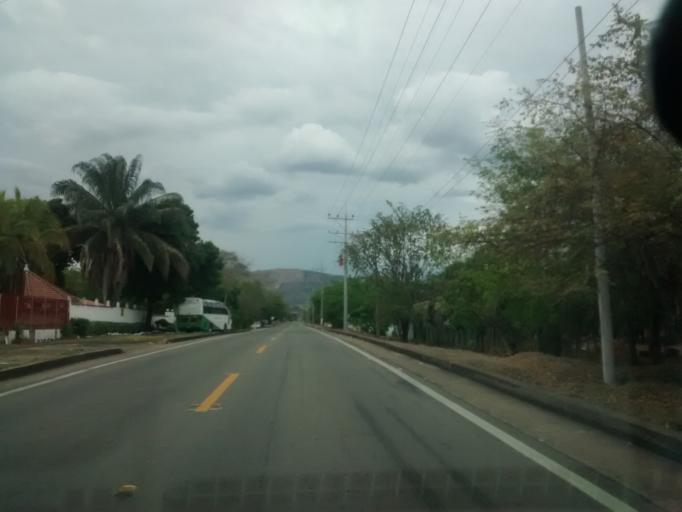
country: CO
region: Cundinamarca
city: Tocaima
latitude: 4.4487
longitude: -74.6564
